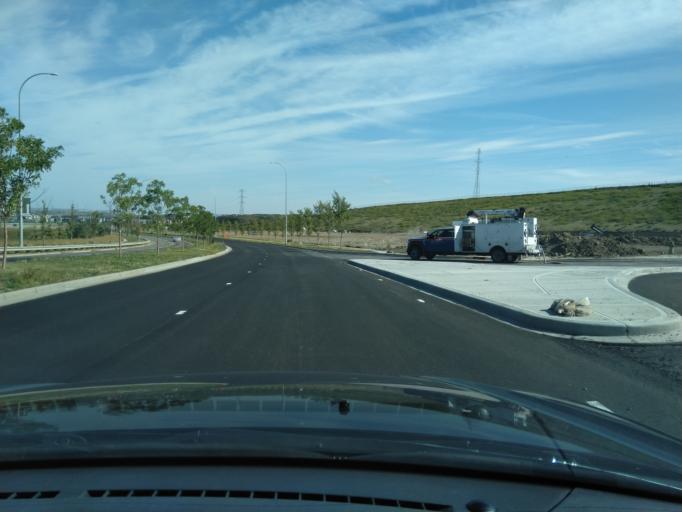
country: CA
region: Alberta
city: Calgary
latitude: 51.1715
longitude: -114.1742
